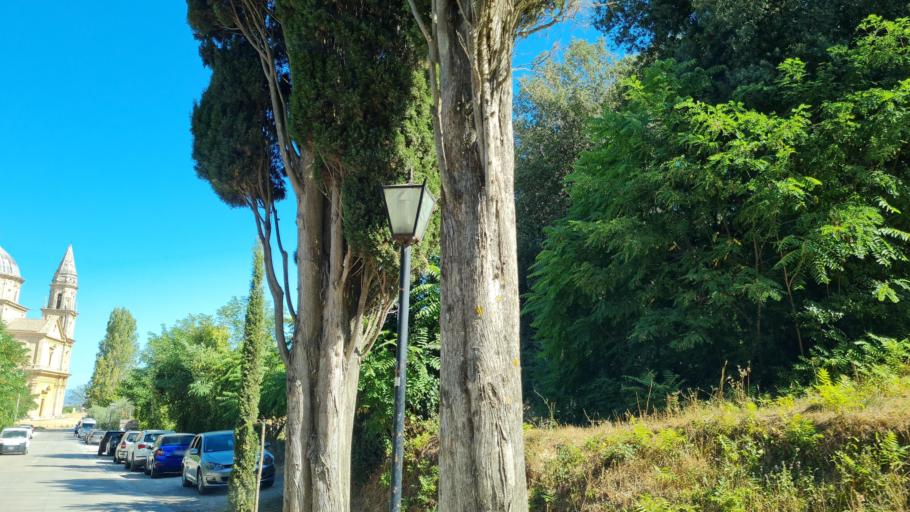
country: IT
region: Tuscany
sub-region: Provincia di Siena
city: Montepulciano
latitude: 43.0890
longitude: 11.7755
